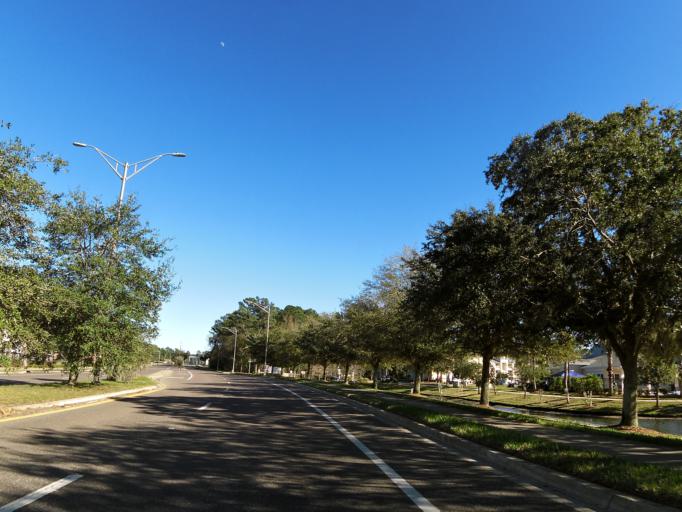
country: US
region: Florida
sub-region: Duval County
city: Jacksonville
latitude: 30.2472
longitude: -81.5604
